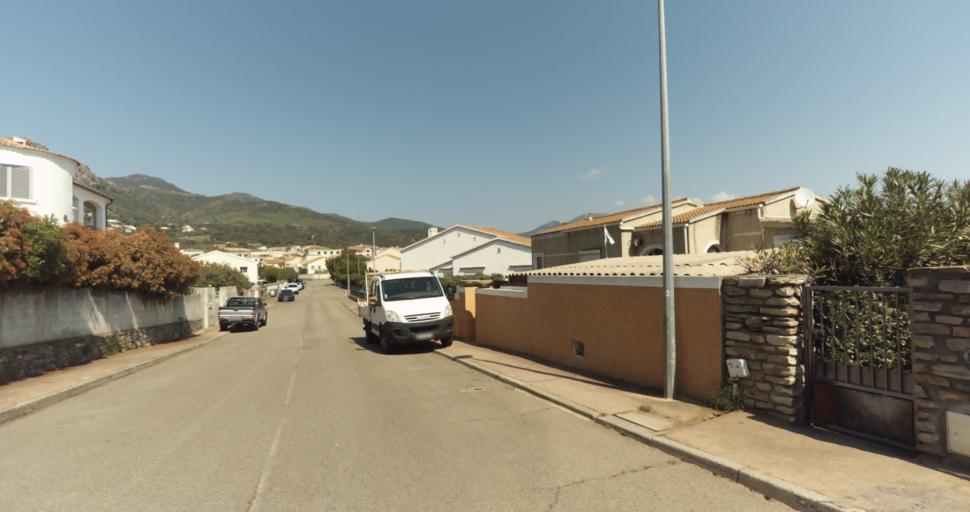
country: FR
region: Corsica
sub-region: Departement de la Haute-Corse
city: Biguglia
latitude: 42.6267
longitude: 9.4335
